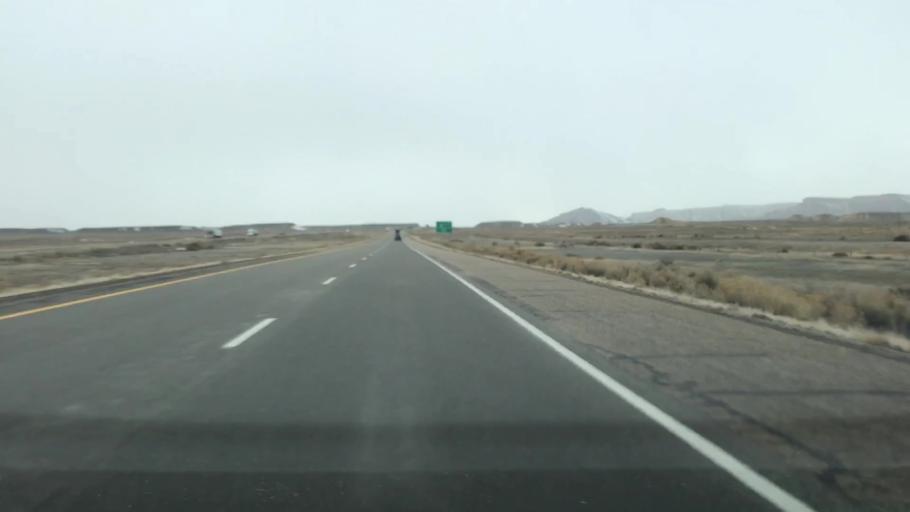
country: US
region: Utah
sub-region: Grand County
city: Moab
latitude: 38.9486
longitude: -109.7867
